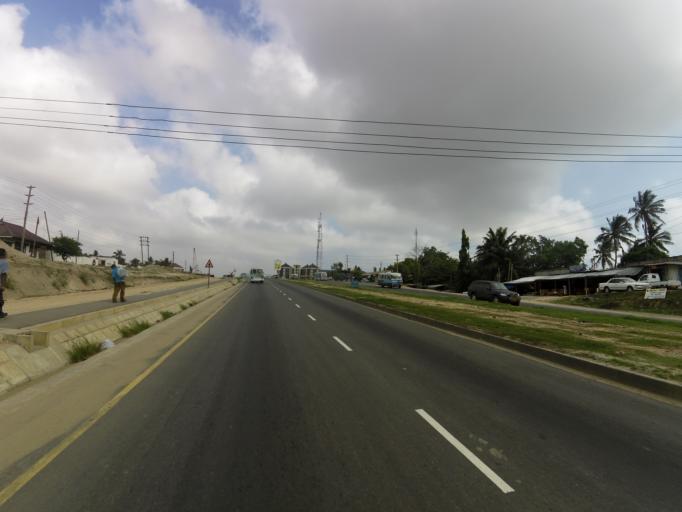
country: TZ
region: Dar es Salaam
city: Magomeni
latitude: -6.7335
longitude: 39.2161
